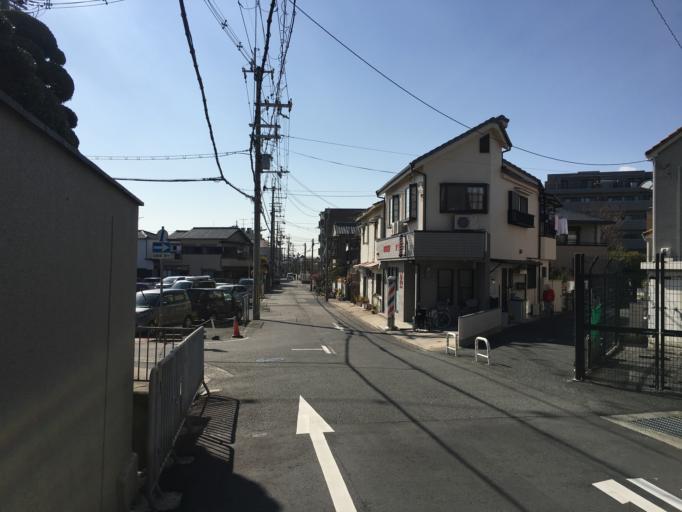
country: JP
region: Hyogo
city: Itami
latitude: 34.7878
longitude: 135.4089
